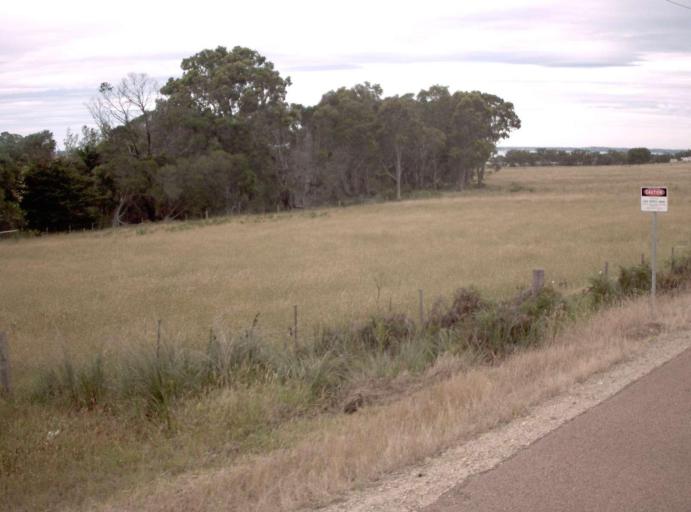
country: AU
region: Victoria
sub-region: East Gippsland
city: Bairnsdale
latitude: -37.9018
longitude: 147.6799
